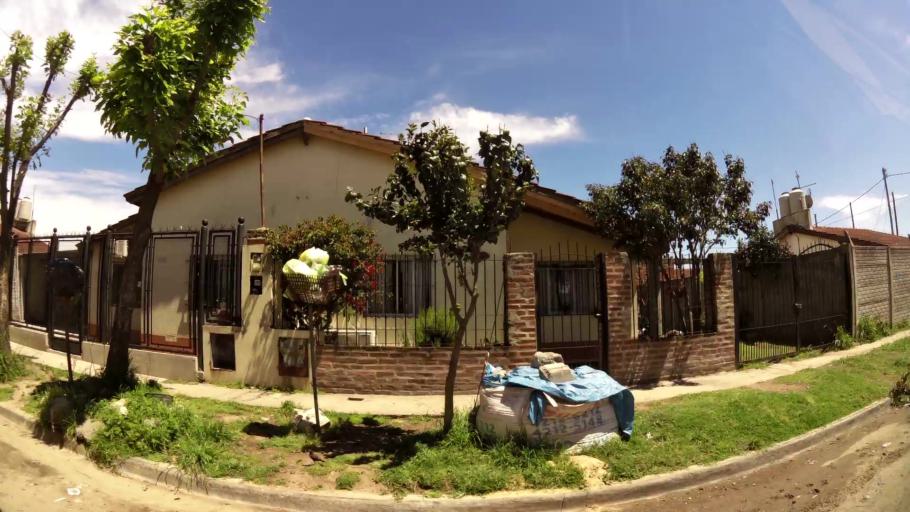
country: AR
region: Buenos Aires
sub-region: Partido de Quilmes
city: Quilmes
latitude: -34.7467
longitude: -58.3088
